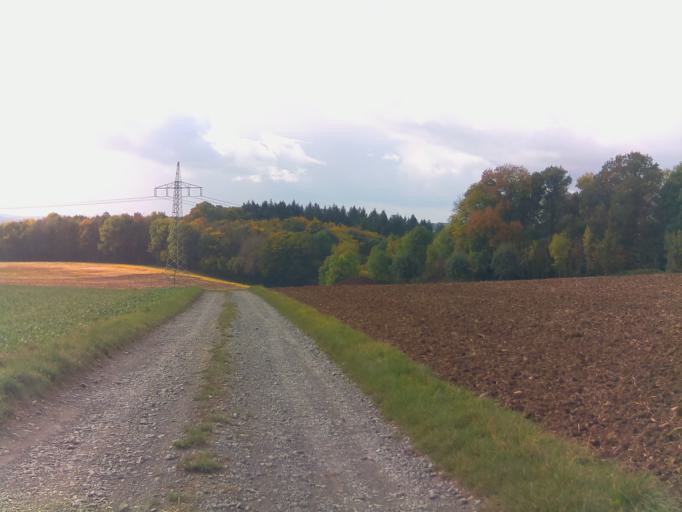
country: DE
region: Baden-Wuerttemberg
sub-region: Regierungsbezirk Stuttgart
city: Grossrinderfeld
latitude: 49.6816
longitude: 9.7152
